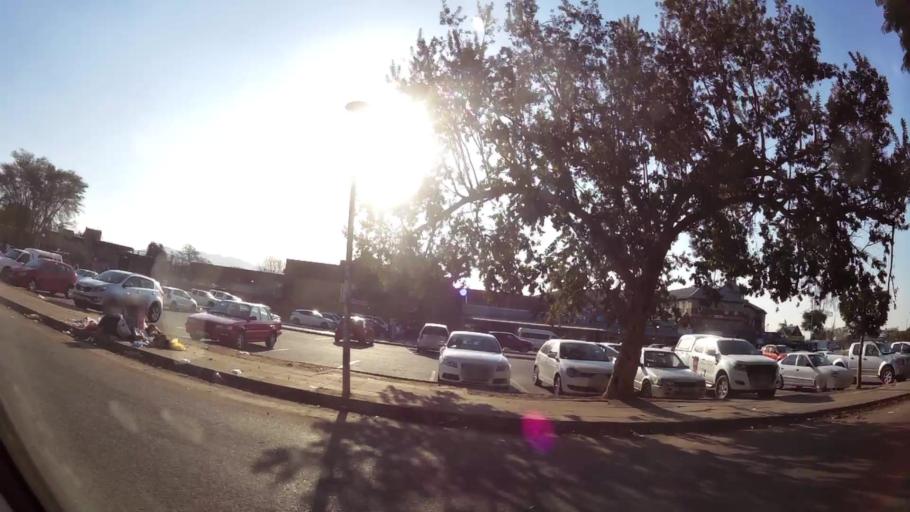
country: ZA
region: North-West
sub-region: Bojanala Platinum District Municipality
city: Rustenburg
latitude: -25.6698
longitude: 27.2385
